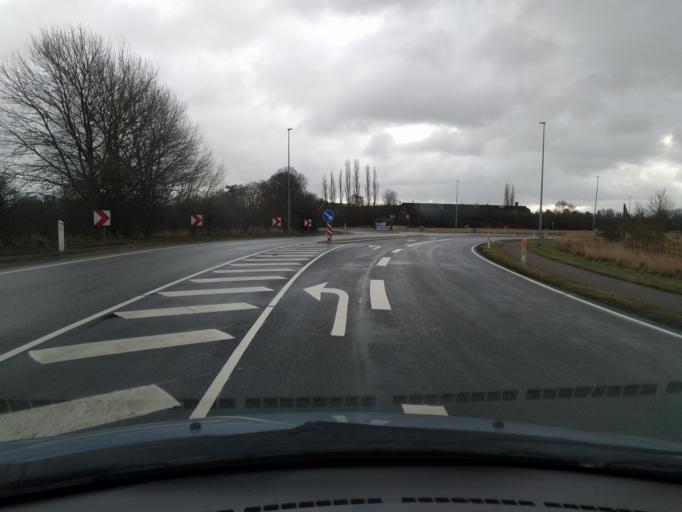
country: DK
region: South Denmark
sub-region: Kerteminde Kommune
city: Langeskov
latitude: 55.3667
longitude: 10.5742
